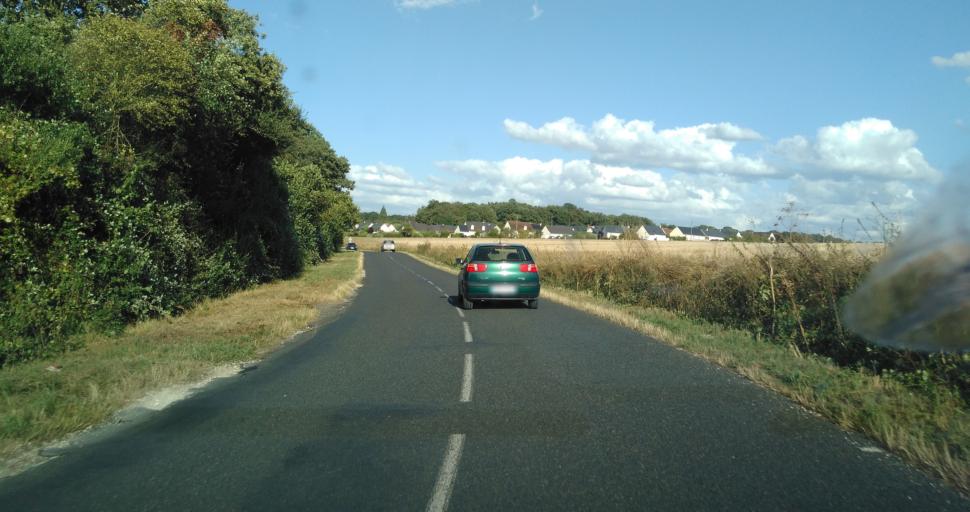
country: FR
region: Centre
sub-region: Departement d'Indre-et-Loire
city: Charge
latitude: 47.4071
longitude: 1.0410
